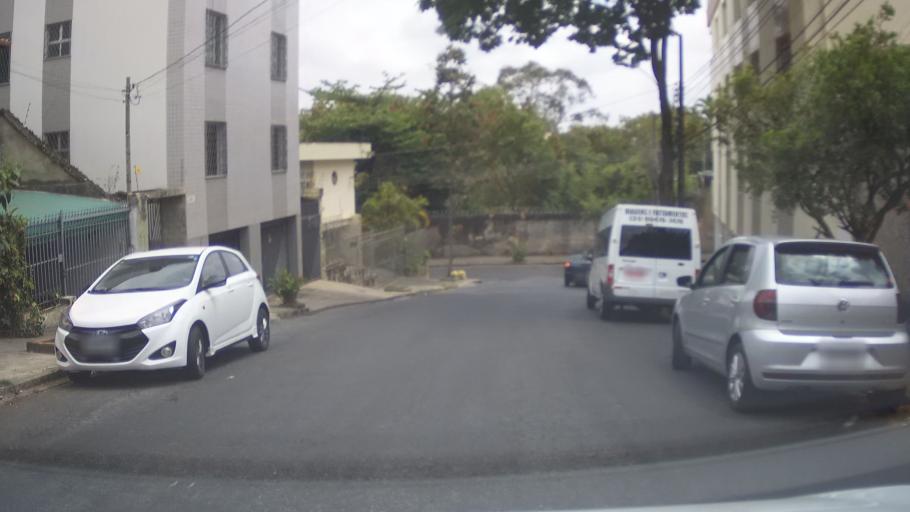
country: BR
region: Minas Gerais
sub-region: Belo Horizonte
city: Belo Horizonte
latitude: -19.8944
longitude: -43.9348
